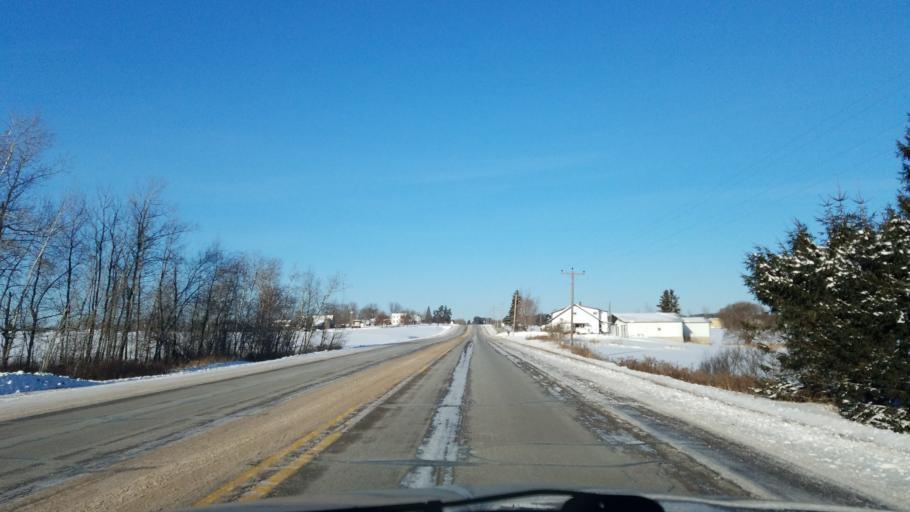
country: US
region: Wisconsin
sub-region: Barron County
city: Cumberland
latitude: 45.5131
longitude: -92.0521
